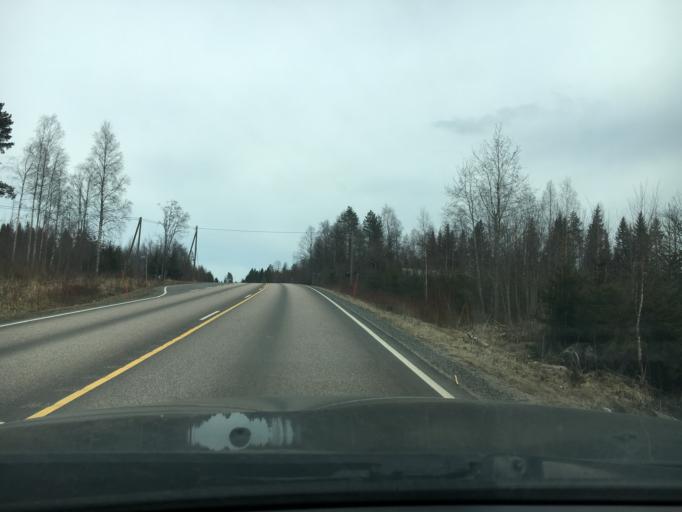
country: FI
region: Central Finland
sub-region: AEaenekoski
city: Konnevesi
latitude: 62.6956
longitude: 26.4315
